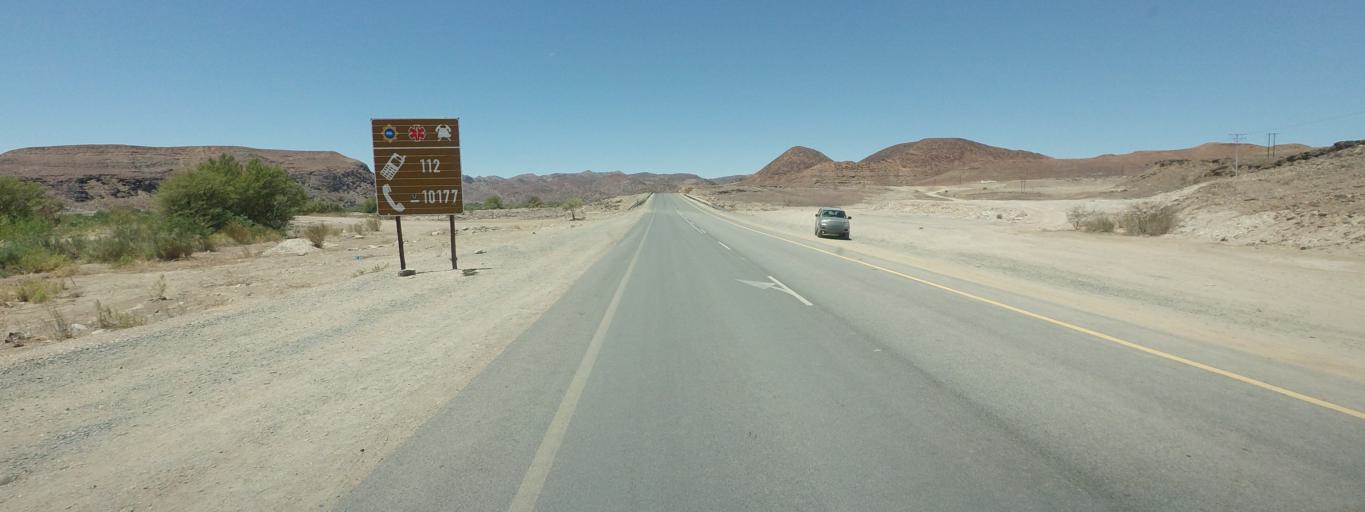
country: ZA
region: Northern Cape
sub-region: Namakwa District Municipality
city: Port Nolloth
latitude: -28.7723
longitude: 17.6297
